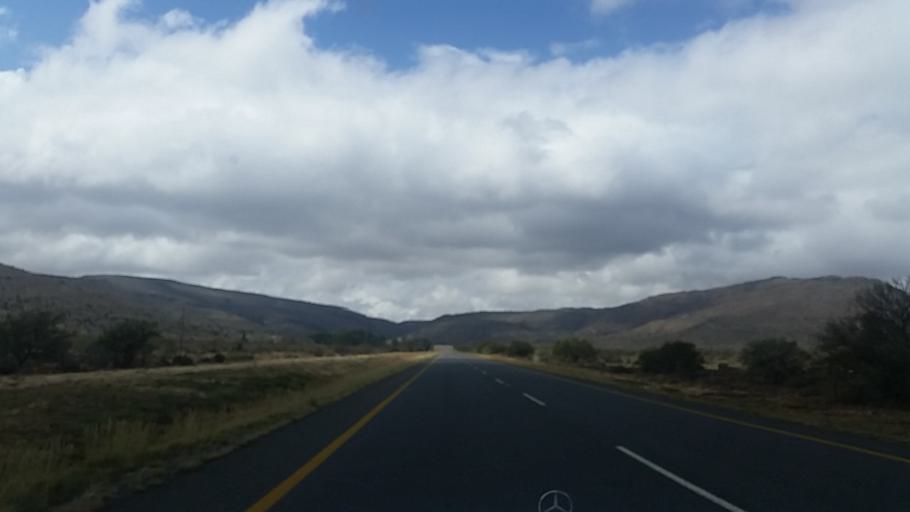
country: ZA
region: Eastern Cape
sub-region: Cacadu District Municipality
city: Graaff-Reinet
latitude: -31.9853
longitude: 24.6925
